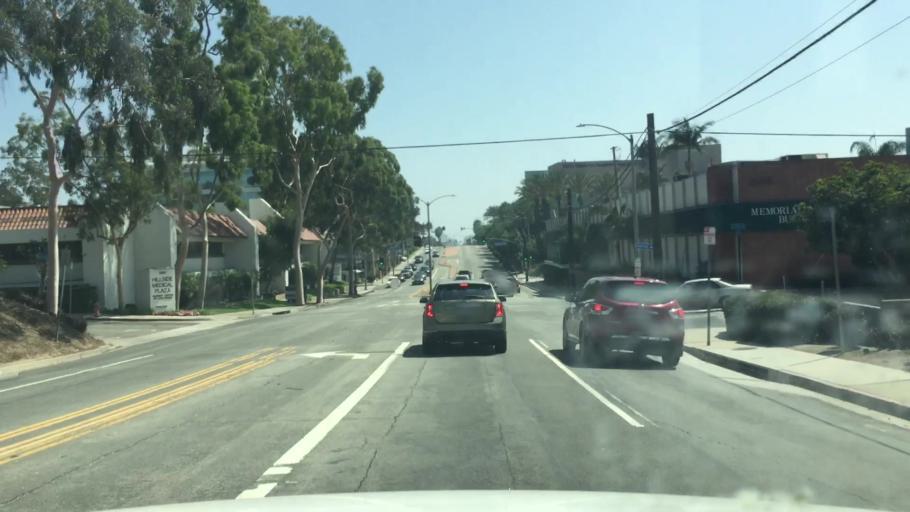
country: US
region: California
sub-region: Los Angeles County
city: Signal Hill
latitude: 33.8102
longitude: -118.1851
